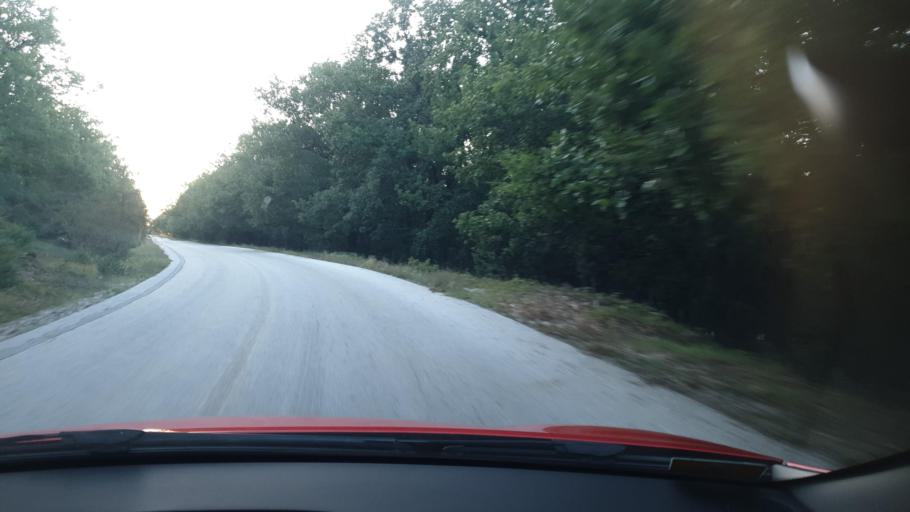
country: GR
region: Central Macedonia
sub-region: Nomos Thessalonikis
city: Peristera
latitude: 40.5162
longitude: 23.2136
